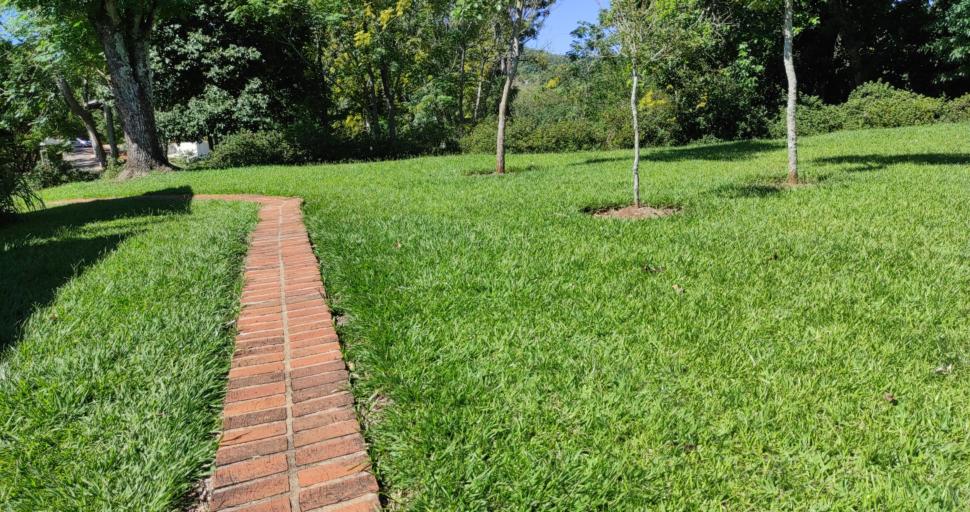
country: AR
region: Misiones
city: El Soberbio
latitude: -27.3051
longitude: -54.1939
